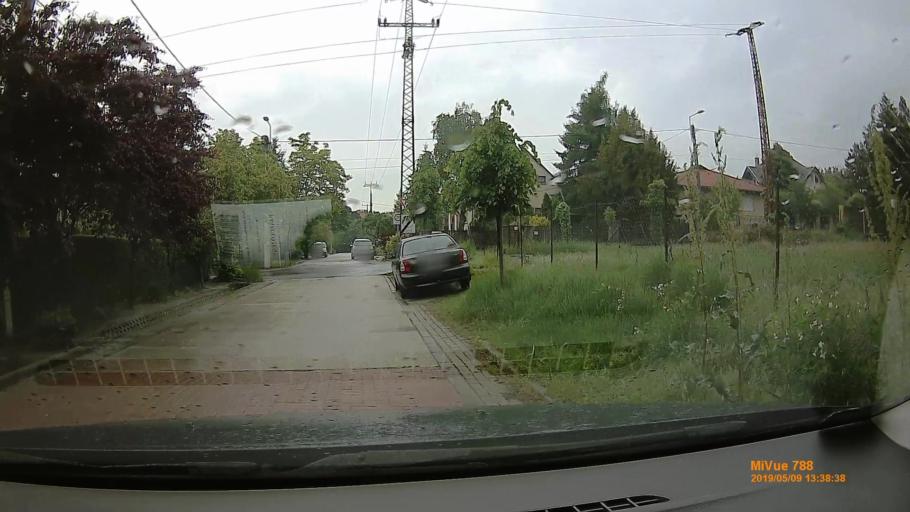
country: HU
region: Budapest
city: Budapest XVI. keruelet
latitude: 47.5303
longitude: 19.1979
